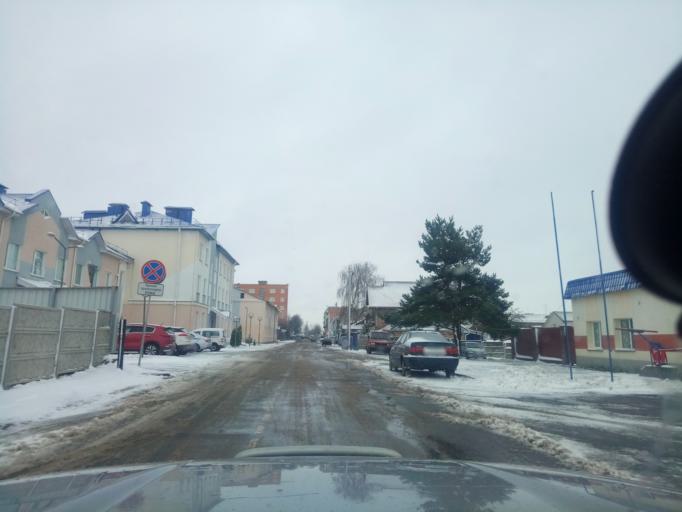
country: BY
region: Minsk
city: Kapyl'
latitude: 53.1528
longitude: 27.0858
